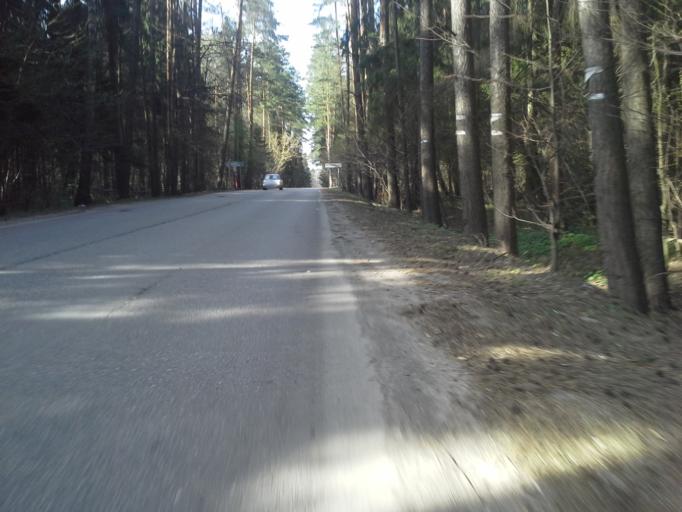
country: RU
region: Moskovskaya
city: Dubrovitsy
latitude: 55.4326
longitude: 37.3990
